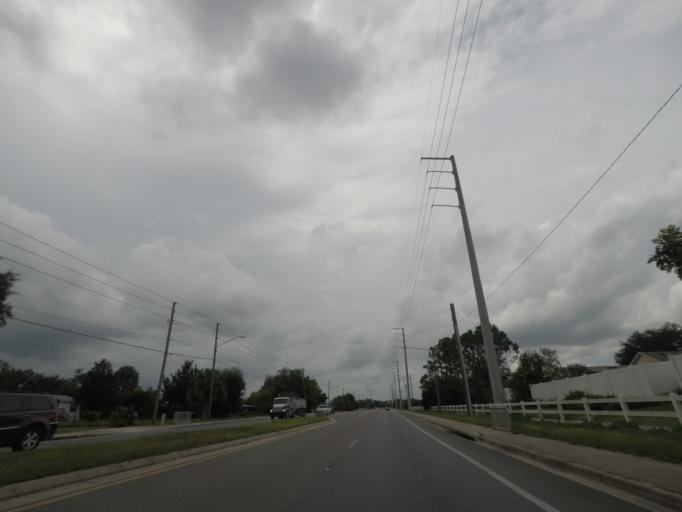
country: US
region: Florida
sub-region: Polk County
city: Loughman
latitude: 28.2450
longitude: -81.5835
